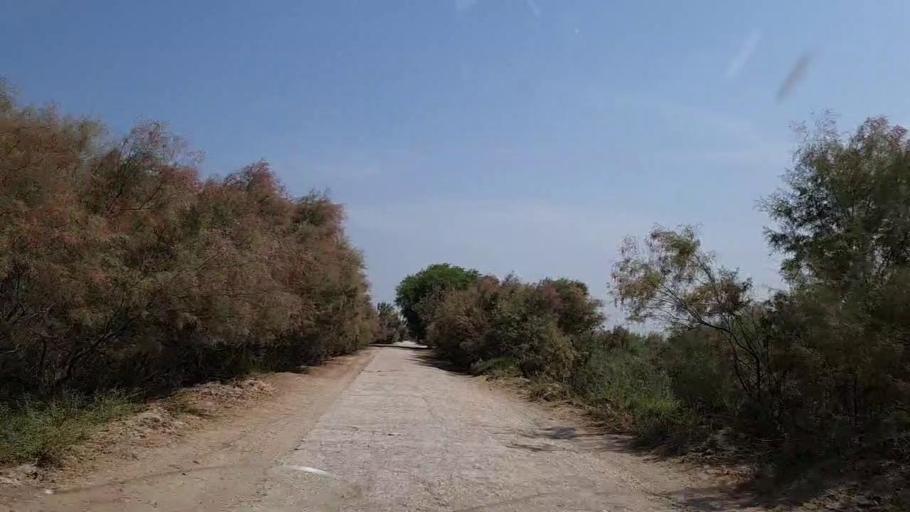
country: PK
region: Sindh
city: Khanpur
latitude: 27.8208
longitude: 69.3041
